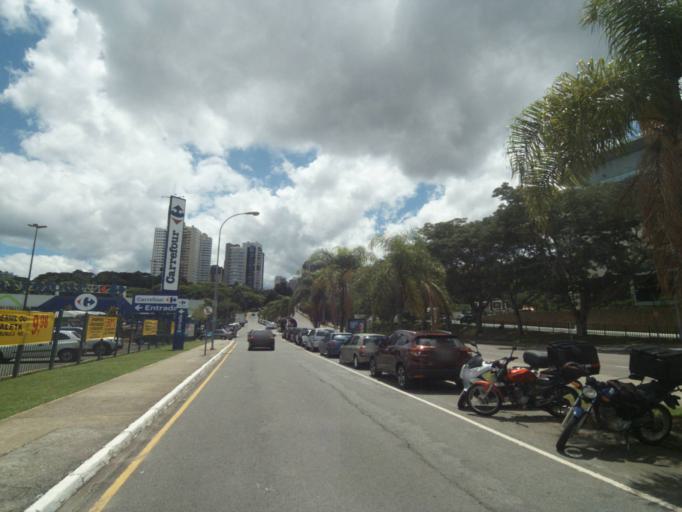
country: BR
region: Parana
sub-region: Curitiba
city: Curitiba
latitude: -25.4365
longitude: -49.3172
